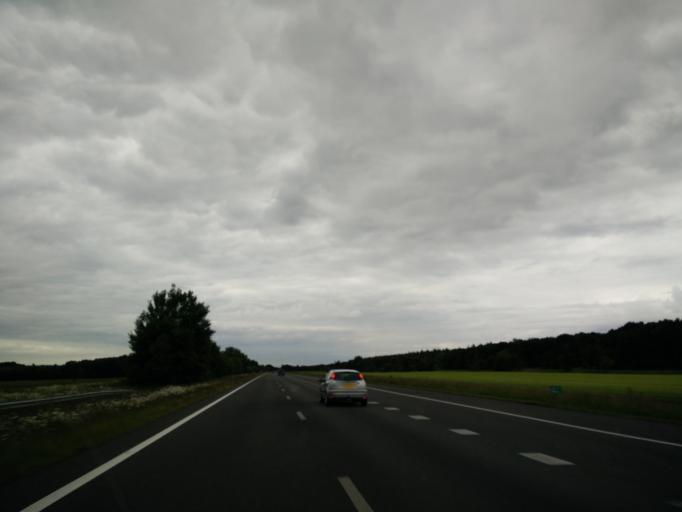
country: NL
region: Drenthe
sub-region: Gemeente Hoogeveen
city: Hoogeveen
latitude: 52.7434
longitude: 6.4629
